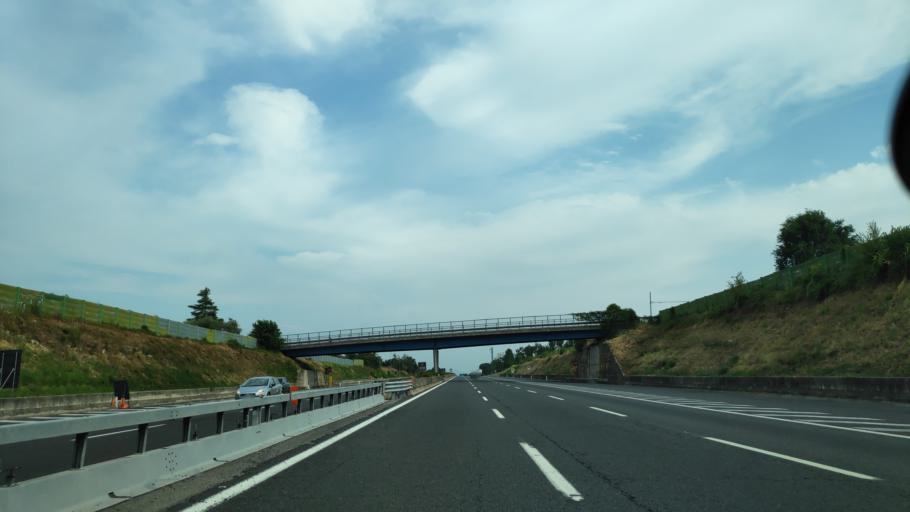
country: IT
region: Latium
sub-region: Citta metropolitana di Roma Capitale
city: Fiano Romano
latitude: 42.1745
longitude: 12.6071
